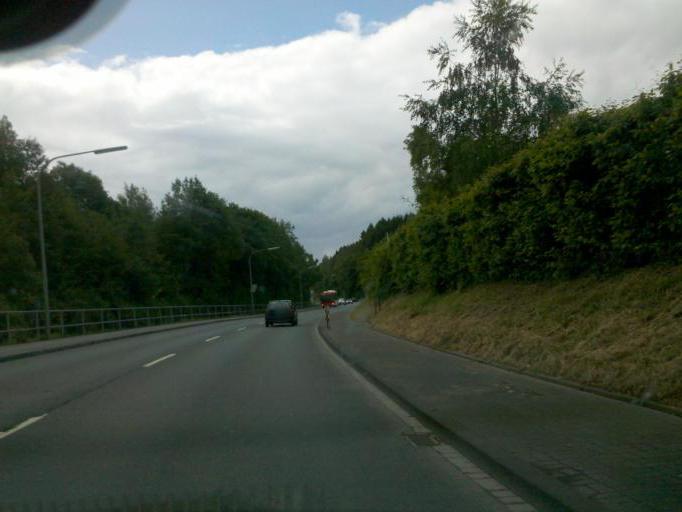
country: DE
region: North Rhine-Westphalia
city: Warstein
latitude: 51.4749
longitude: 8.3386
